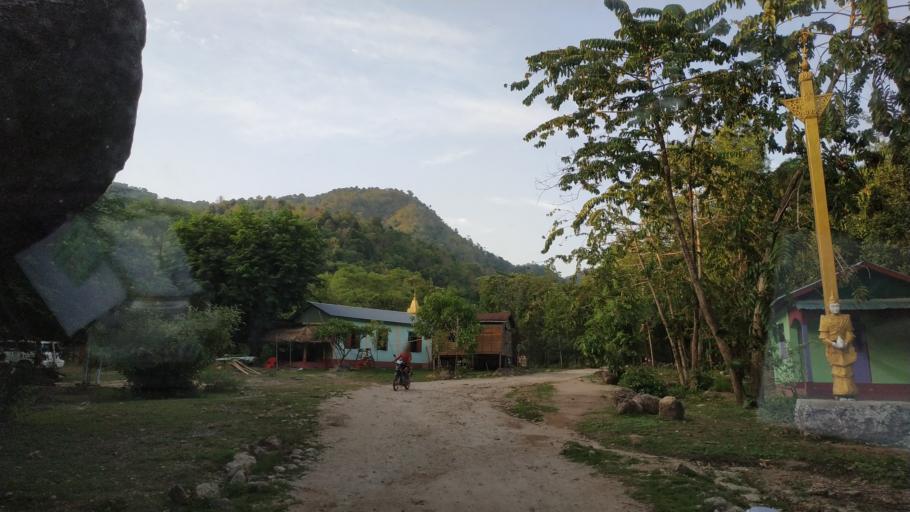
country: MM
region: Mon
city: Kyaikto
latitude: 17.4403
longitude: 97.0415
